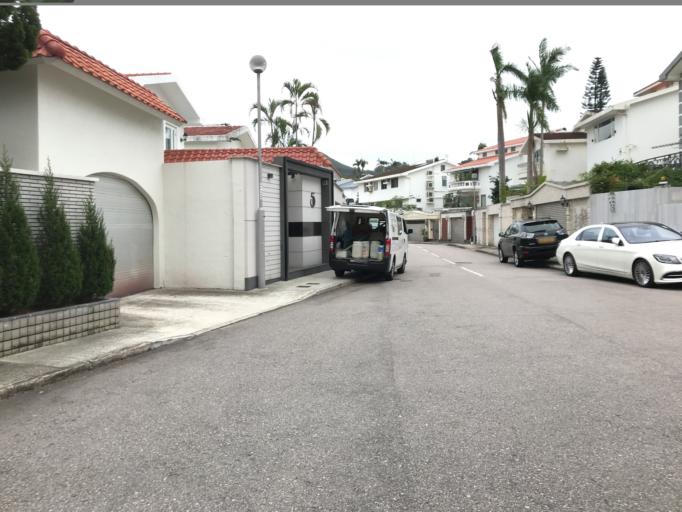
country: HK
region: Tai Po
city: Tai Po
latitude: 22.4601
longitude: 114.1516
